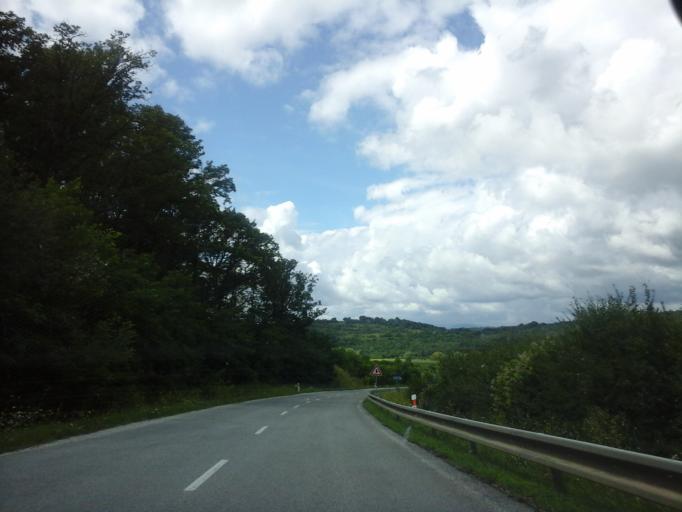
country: SK
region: Kosicky
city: Roznava
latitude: 48.5238
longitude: 20.4106
